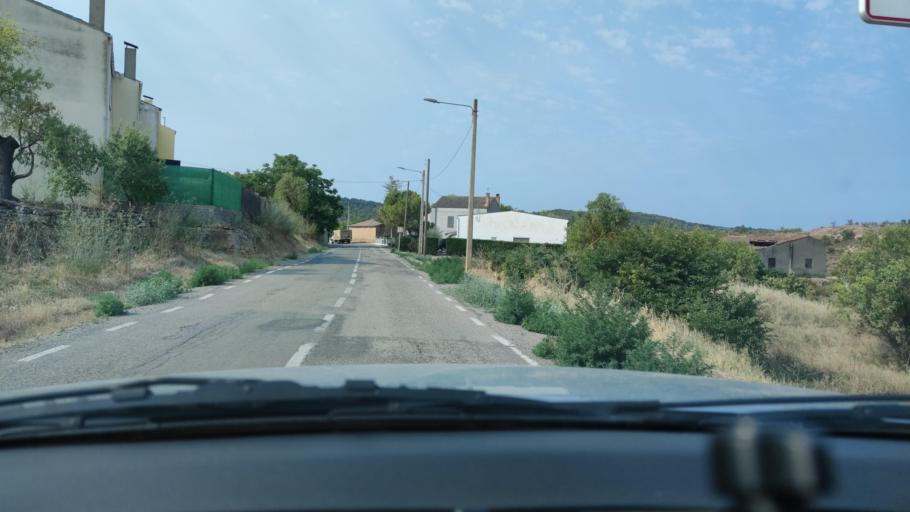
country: ES
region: Catalonia
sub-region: Provincia de Lleida
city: Juncosa
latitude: 41.4284
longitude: 0.8602
